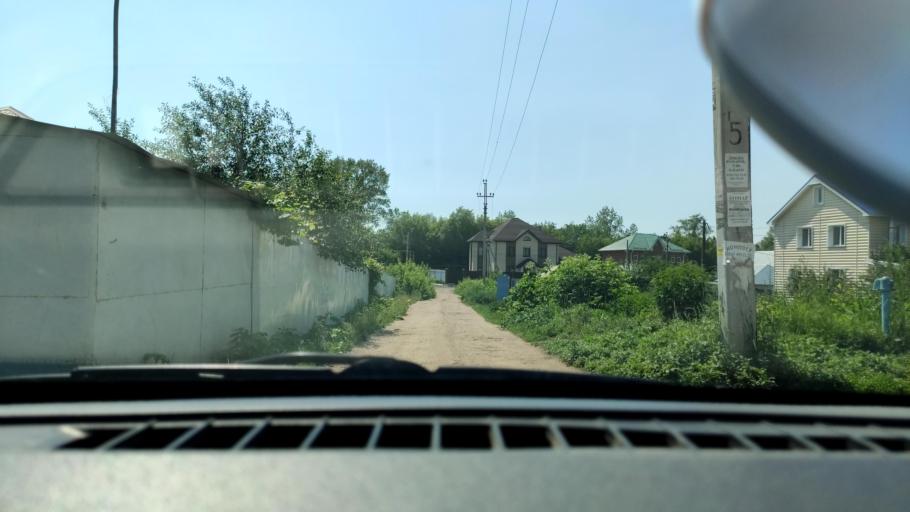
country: RU
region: Samara
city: Novokuybyshevsk
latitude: 53.1448
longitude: 49.9819
